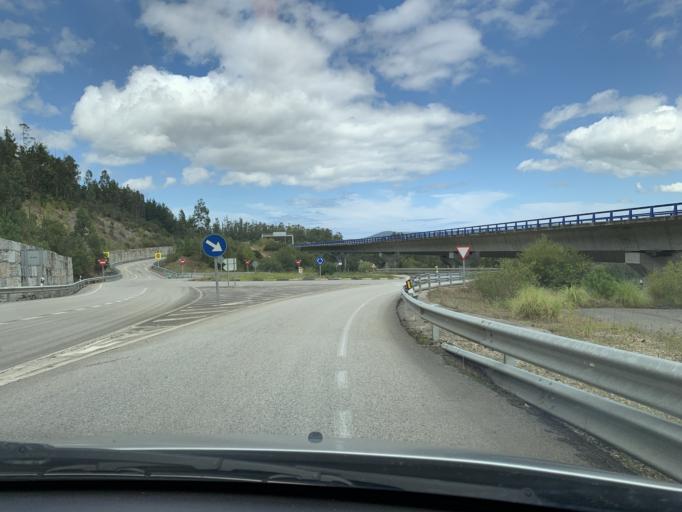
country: ES
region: Galicia
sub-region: Provincia de Lugo
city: Barreiros
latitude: 43.4681
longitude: -7.3151
